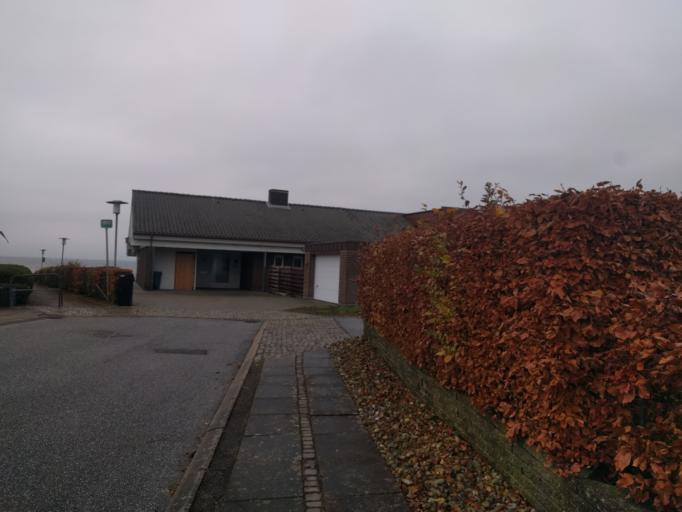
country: DK
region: South Denmark
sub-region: Fredericia Kommune
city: Snoghoj
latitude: 55.5408
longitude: 9.7286
